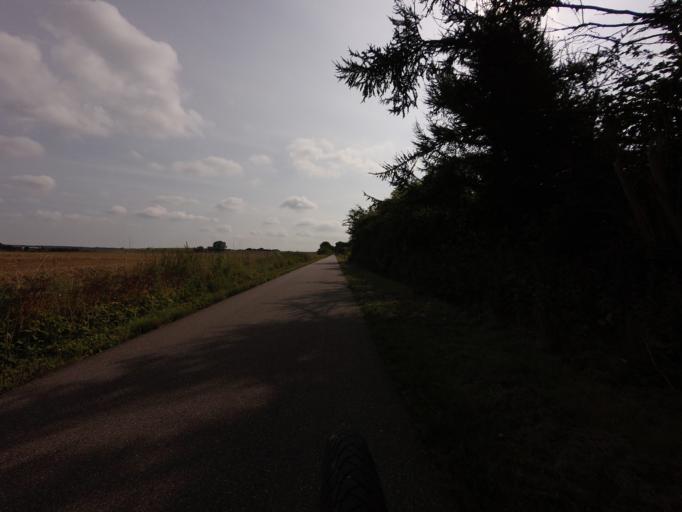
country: DK
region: Zealand
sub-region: Naestved Kommune
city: Naestved
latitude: 55.2525
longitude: 11.7195
